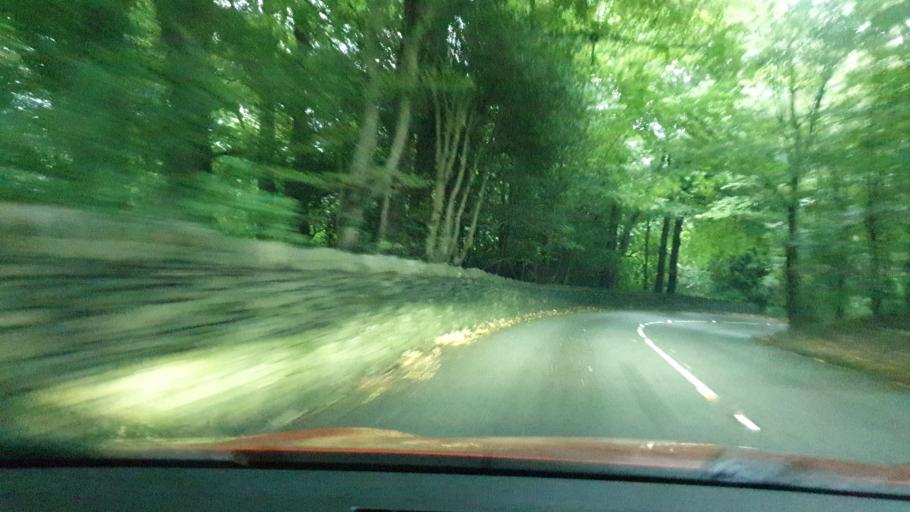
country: GB
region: England
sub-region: Cumbria
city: Ulverston
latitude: 54.2515
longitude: -3.0703
